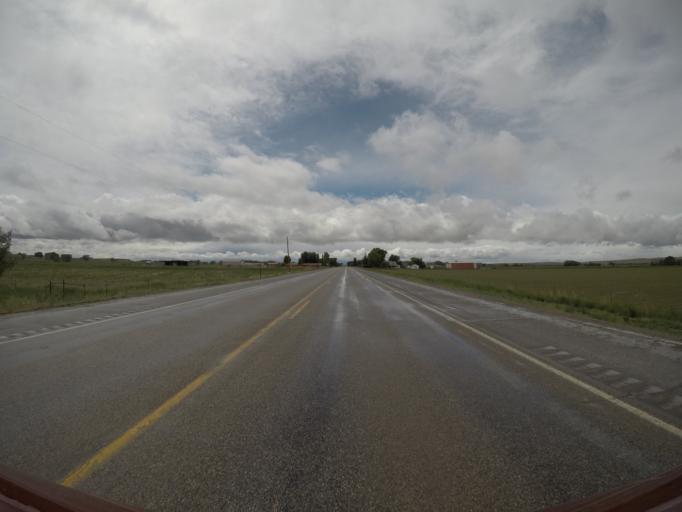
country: US
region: Wyoming
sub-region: Big Horn County
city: Lovell
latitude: 44.8407
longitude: -108.3383
